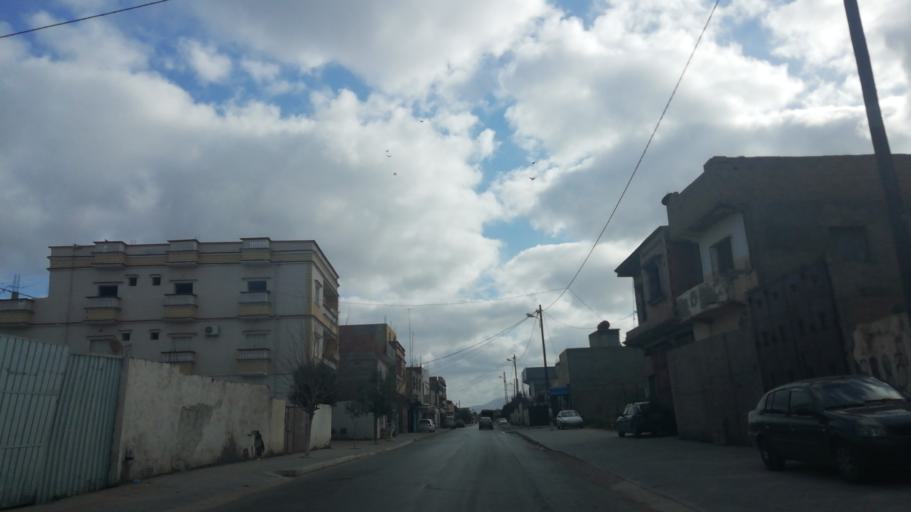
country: DZ
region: Relizane
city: Mazouna
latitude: 36.2599
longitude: 0.6055
